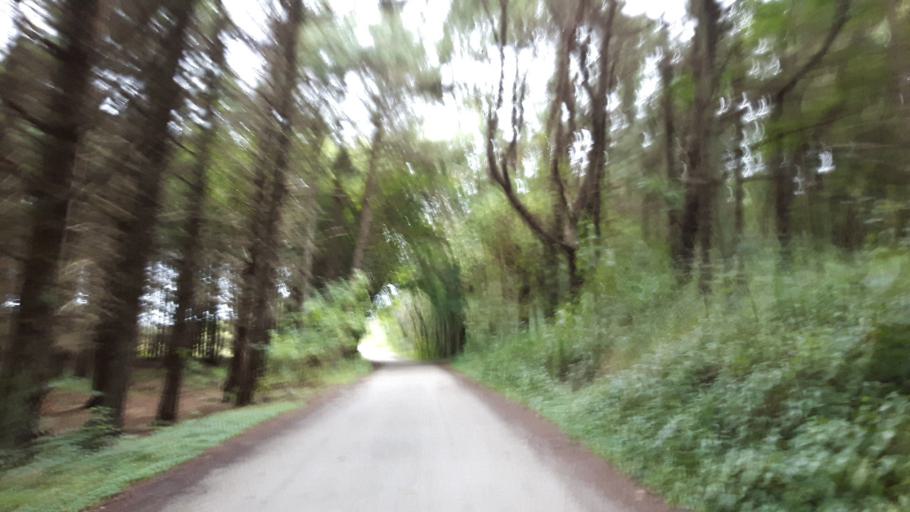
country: NL
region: Friesland
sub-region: Gemeente Ameland
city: Nes
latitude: 53.4545
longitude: 5.7570
